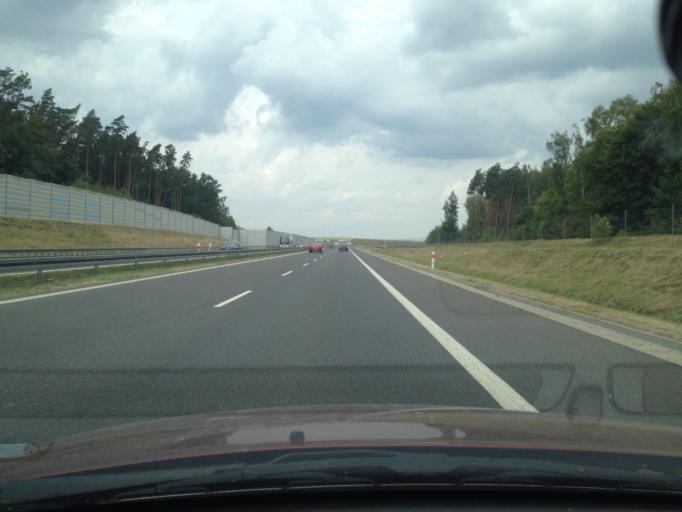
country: PL
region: West Pomeranian Voivodeship
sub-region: Powiat mysliborski
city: Mysliborz
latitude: 52.9706
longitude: 14.9116
